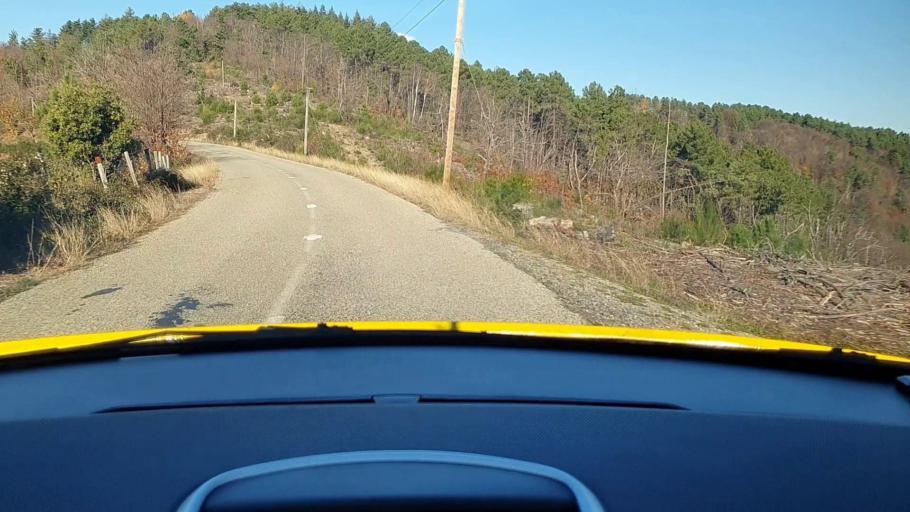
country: FR
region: Languedoc-Roussillon
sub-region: Departement du Gard
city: Branoux-les-Taillades
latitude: 44.2801
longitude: 3.9594
